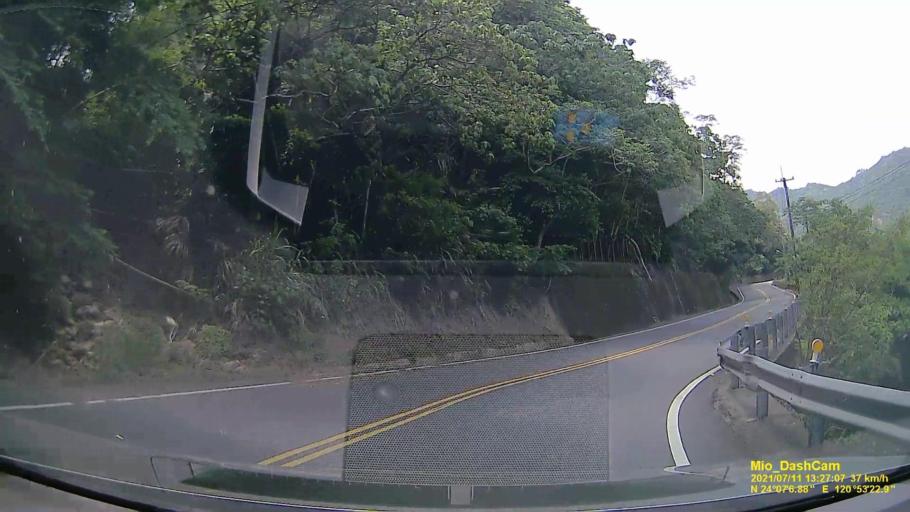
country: TW
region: Taiwan
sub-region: Nantou
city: Puli
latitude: 24.1186
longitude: 120.8897
